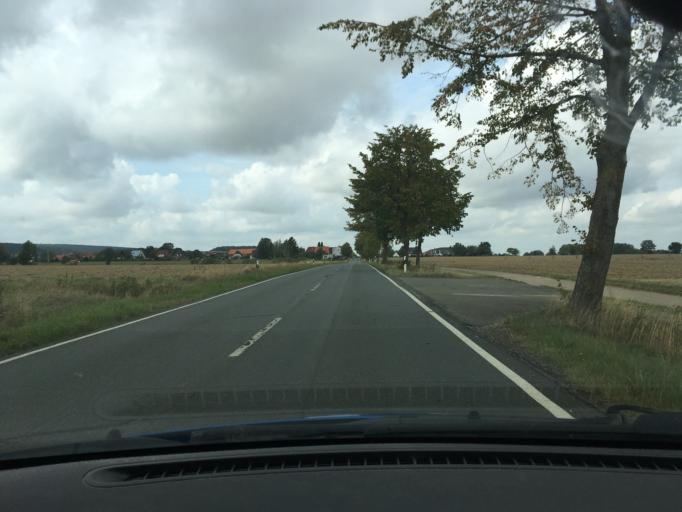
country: DE
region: Lower Saxony
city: Messenkamp
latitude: 52.2022
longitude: 9.4013
